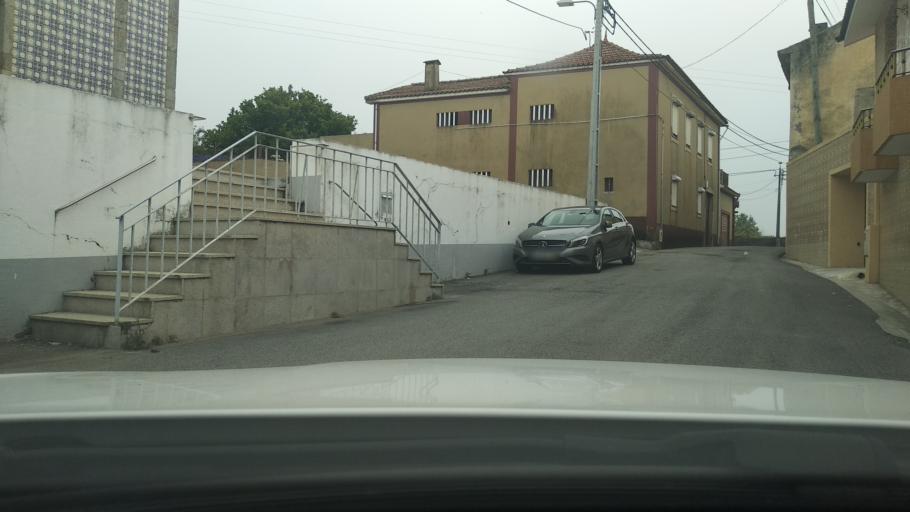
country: PT
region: Aveiro
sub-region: Espinho
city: Silvalde
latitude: 40.9970
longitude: -8.6311
